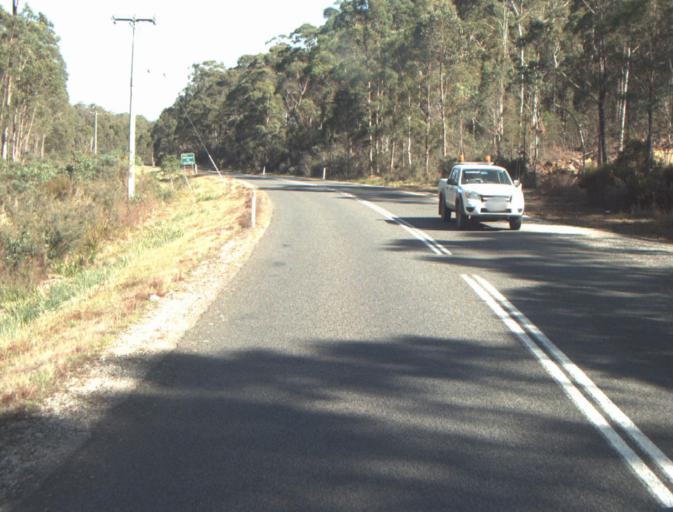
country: AU
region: Tasmania
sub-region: Launceston
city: Mayfield
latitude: -41.3306
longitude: 147.1798
